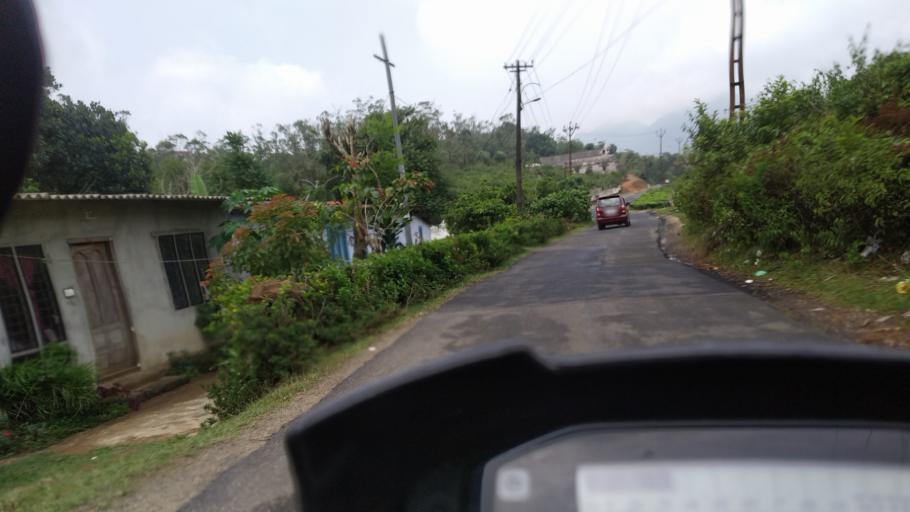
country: IN
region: Kerala
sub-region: Kottayam
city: Erattupetta
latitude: 9.6345
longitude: 76.9571
